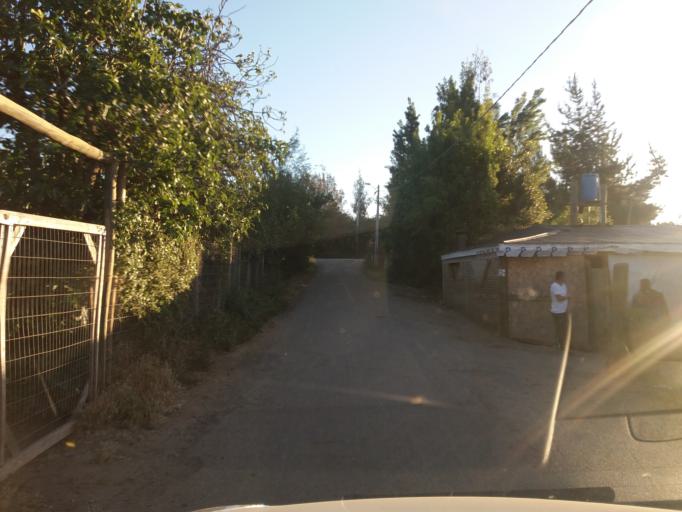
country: CL
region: Valparaiso
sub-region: Provincia de Quillota
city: Quillota
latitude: -32.9468
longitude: -71.2747
